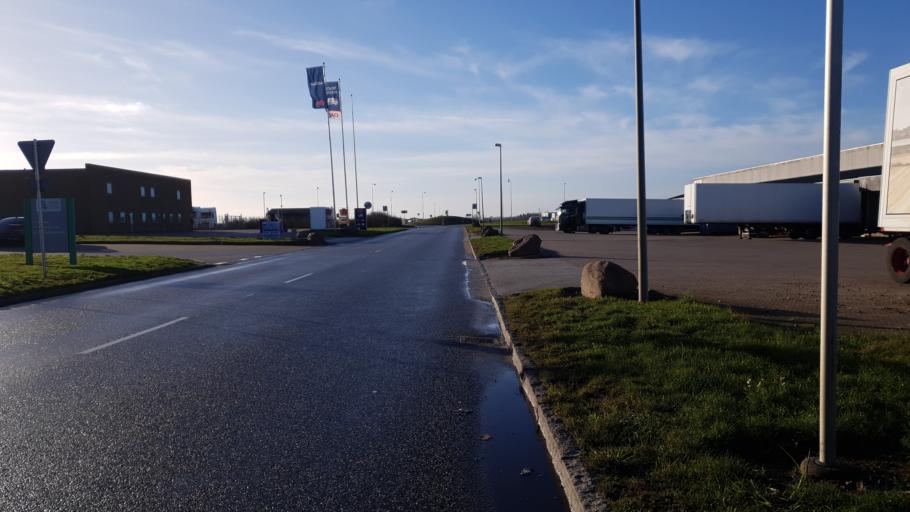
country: DK
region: Central Jutland
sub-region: Hedensted Kommune
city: Hedensted
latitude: 55.7903
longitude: 9.6745
